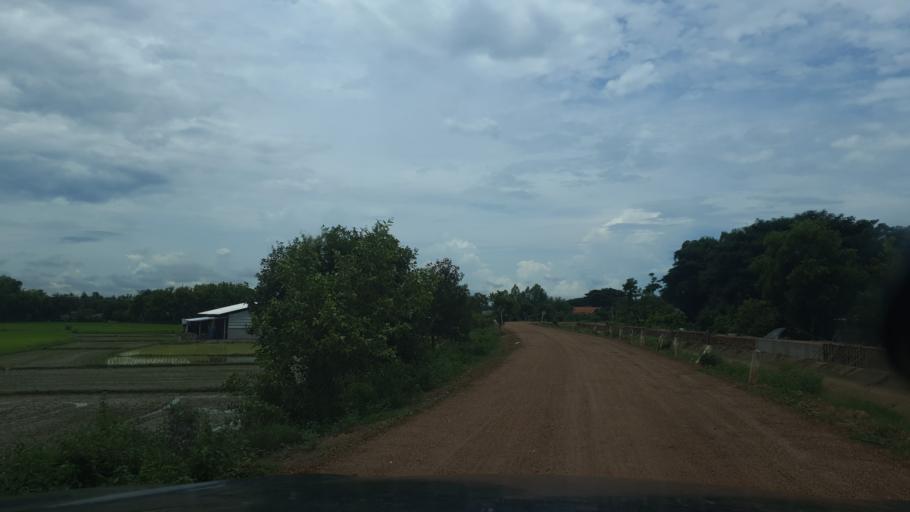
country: TH
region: Lampang
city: Hang Chat
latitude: 18.2898
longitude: 99.3725
